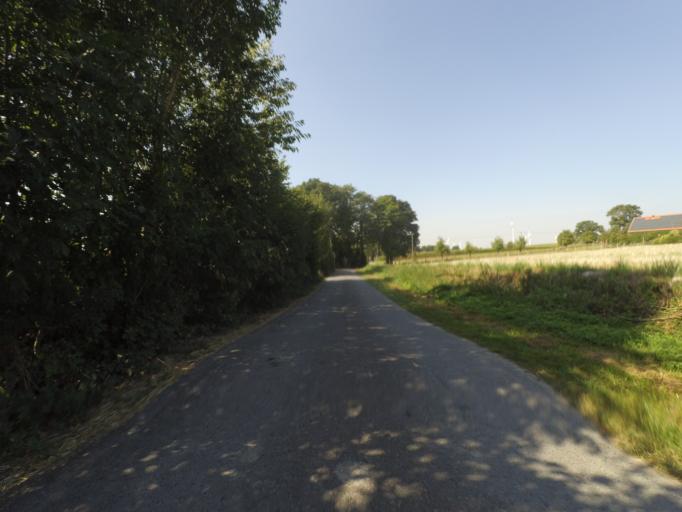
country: DE
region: North Rhine-Westphalia
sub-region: Regierungsbezirk Munster
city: Schoppingen
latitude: 52.0710
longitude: 7.1700
